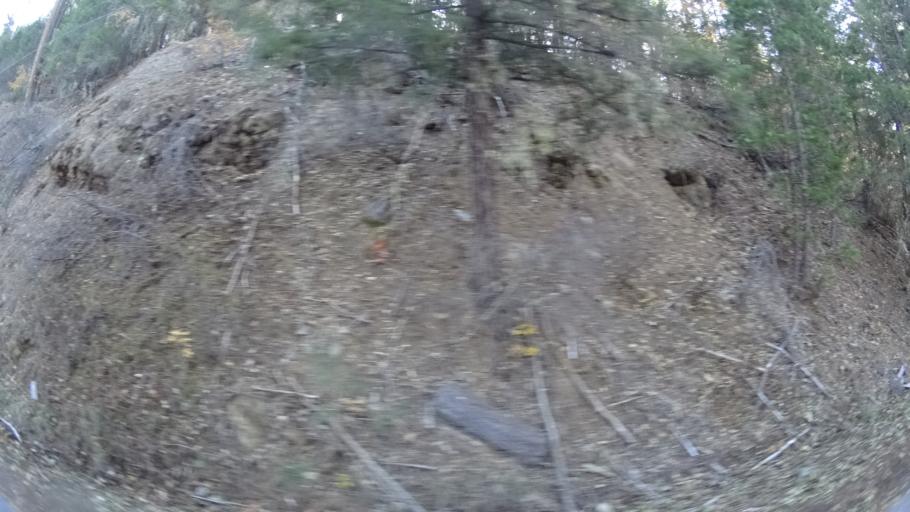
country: US
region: California
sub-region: Siskiyou County
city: Yreka
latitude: 41.8221
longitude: -122.9629
